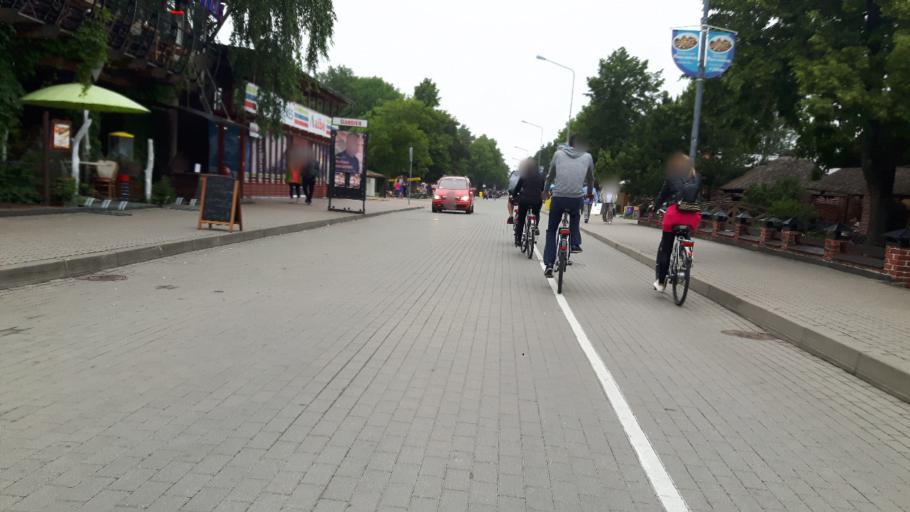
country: LT
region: Klaipedos apskritis
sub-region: Palanga
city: Sventoji
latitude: 56.0306
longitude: 21.0805
